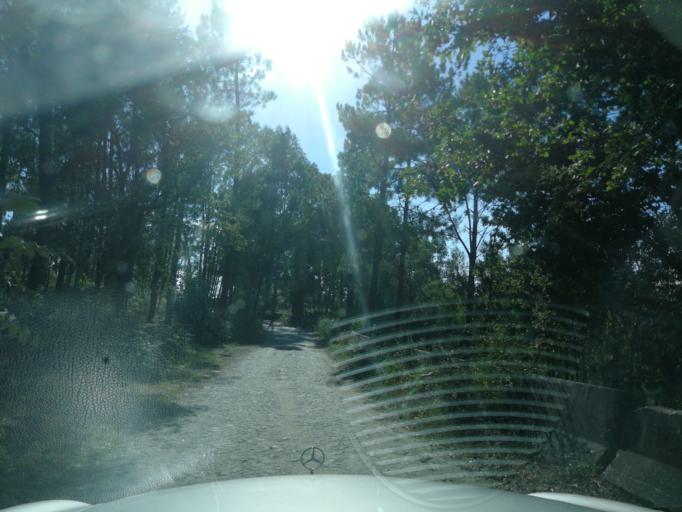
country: PT
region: Braga
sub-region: Braga
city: Adaufe
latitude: 41.5759
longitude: -8.3810
